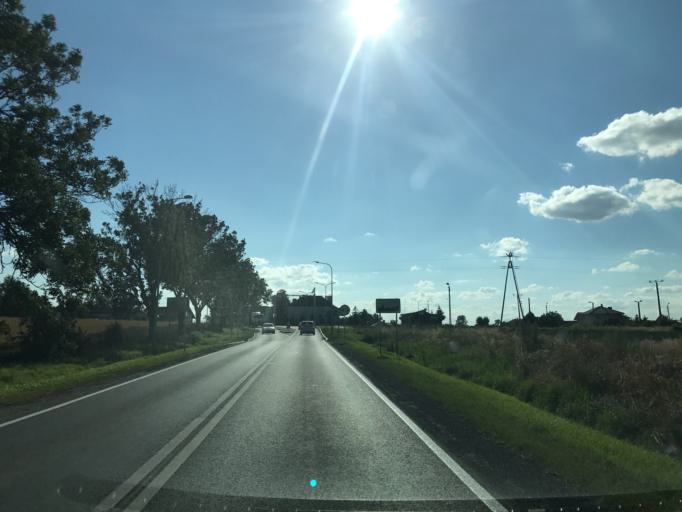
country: PL
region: Kujawsko-Pomorskie
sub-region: Powiat wloclawski
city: Brzesc Kujawski
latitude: 52.6121
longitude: 18.9048
